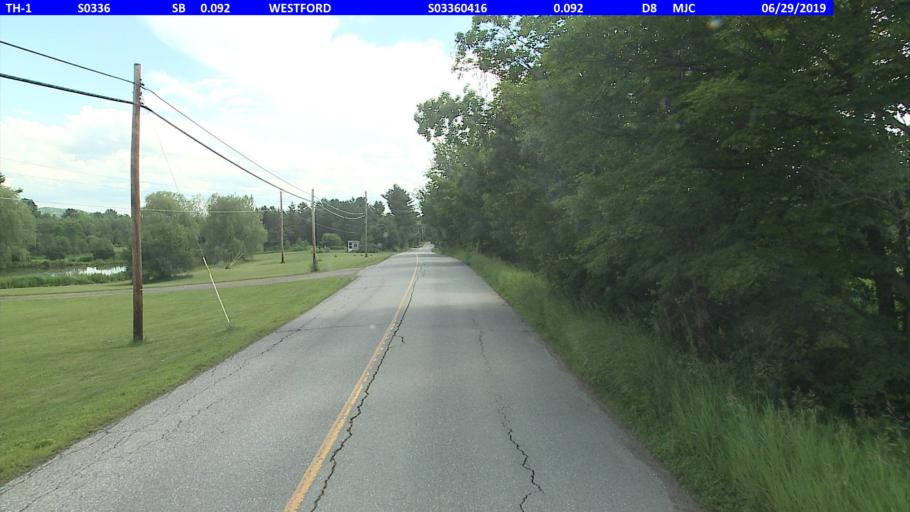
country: US
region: Vermont
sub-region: Chittenden County
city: Milton
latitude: 44.5660
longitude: -73.0617
